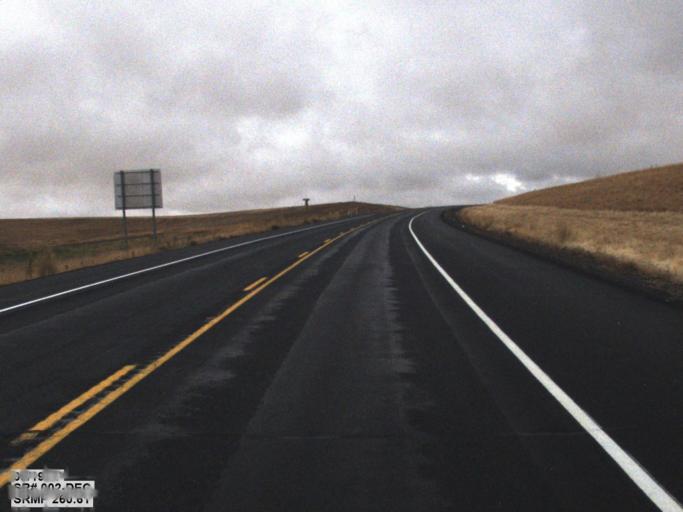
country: US
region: Washington
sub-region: Lincoln County
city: Davenport
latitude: 47.6586
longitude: -117.9477
